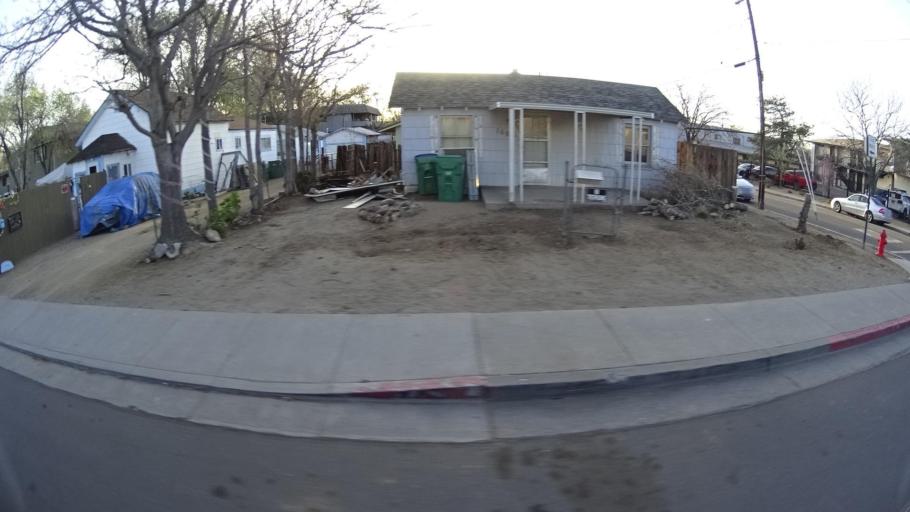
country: US
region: Nevada
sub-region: Washoe County
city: Reno
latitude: 39.5084
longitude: -119.8005
